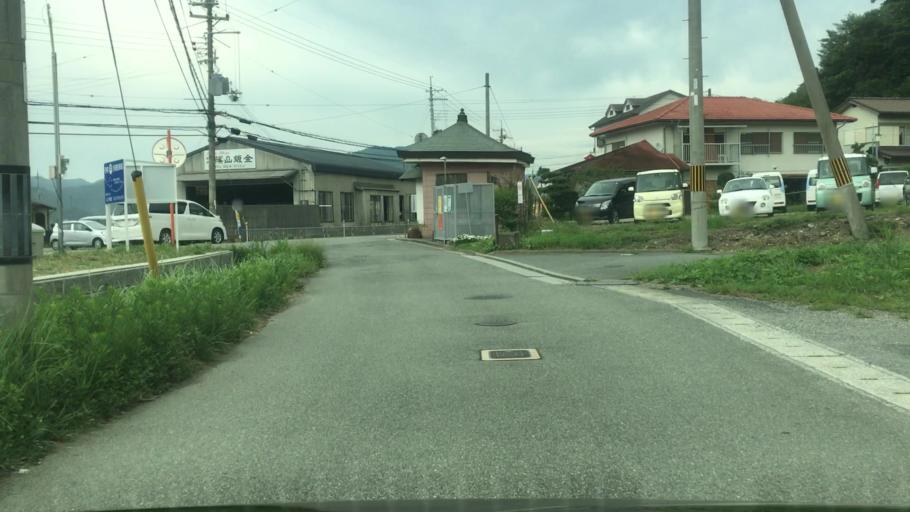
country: JP
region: Hyogo
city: Sasayama
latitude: 35.0652
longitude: 135.1932
